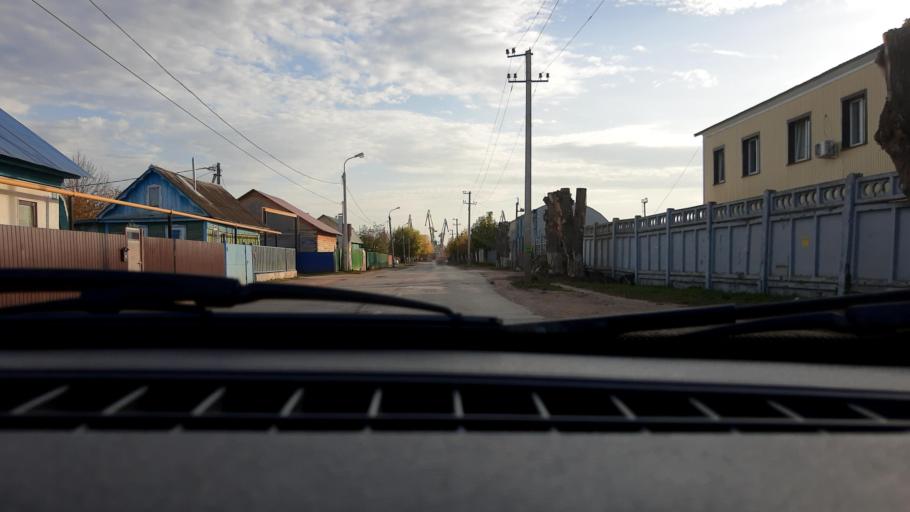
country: RU
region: Bashkortostan
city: Mikhaylovka
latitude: 54.7339
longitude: 55.8966
